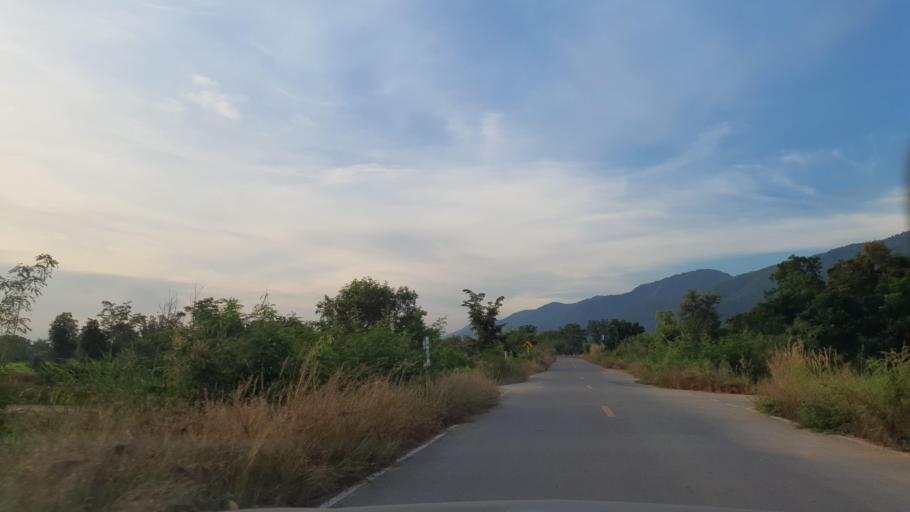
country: TH
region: Uthai Thani
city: Sawang Arom
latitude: 15.7002
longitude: 99.9604
